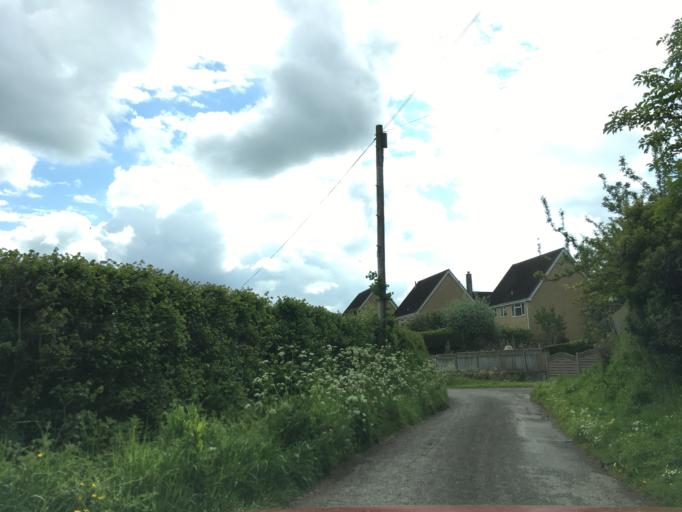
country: GB
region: England
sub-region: Gloucestershire
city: Stonehouse
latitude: 51.7740
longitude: -2.3242
